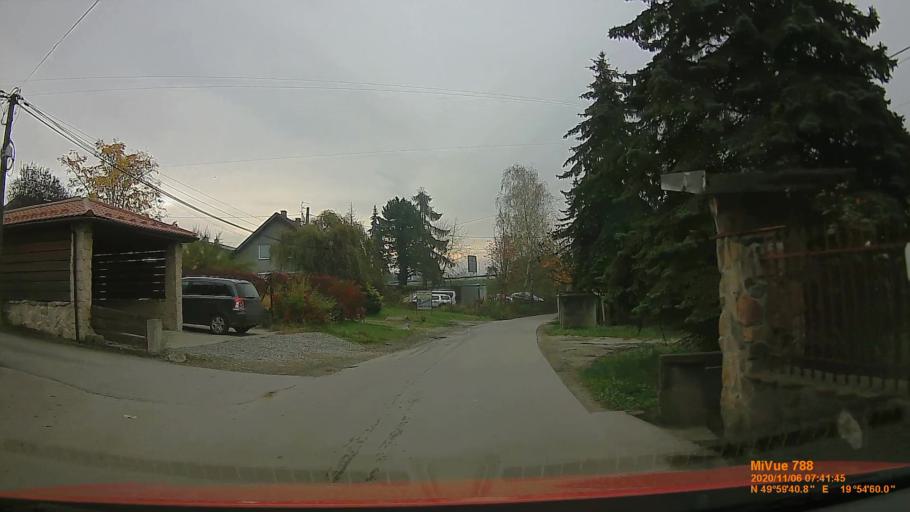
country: PL
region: Lesser Poland Voivodeship
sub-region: Powiat krakowski
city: Libertow
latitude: 49.9947
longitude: 19.9166
